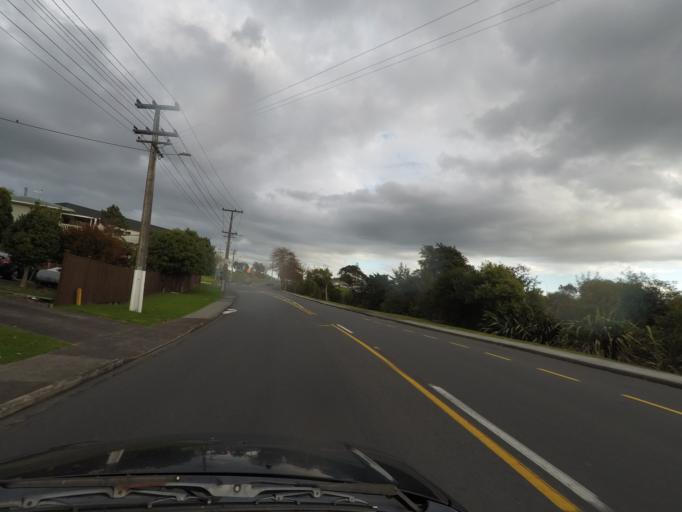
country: NZ
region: Auckland
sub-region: Auckland
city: Rosebank
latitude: -36.8311
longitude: 174.6219
